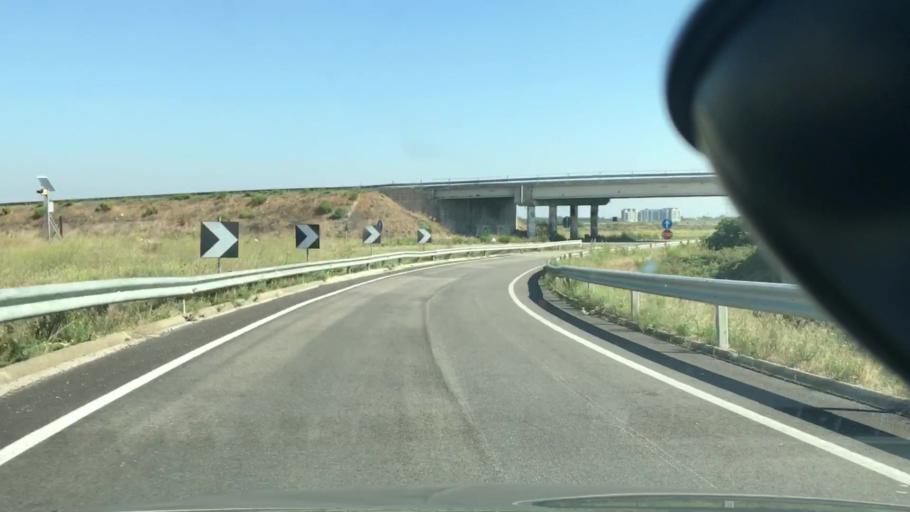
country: IT
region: Apulia
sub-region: Provincia di Foggia
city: Foggia
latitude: 41.4255
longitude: 15.5607
